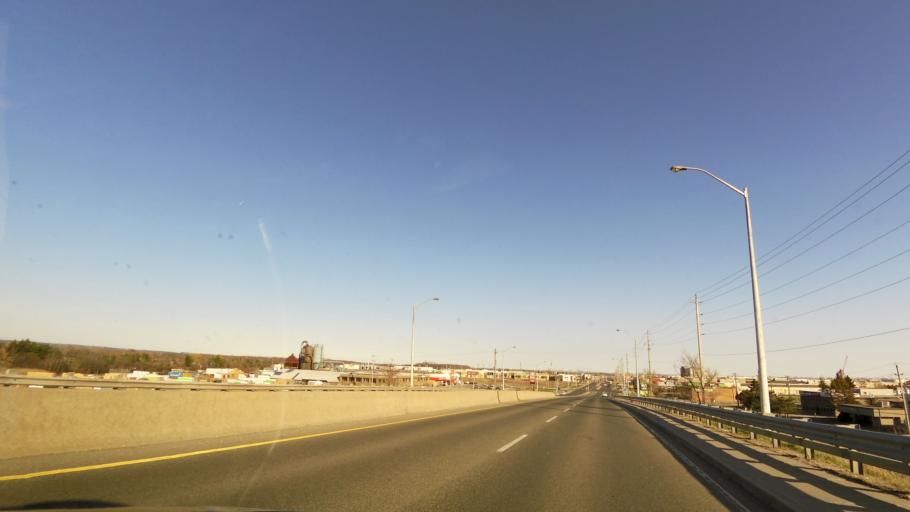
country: CA
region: Ontario
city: Brampton
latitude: 43.8658
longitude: -79.7194
